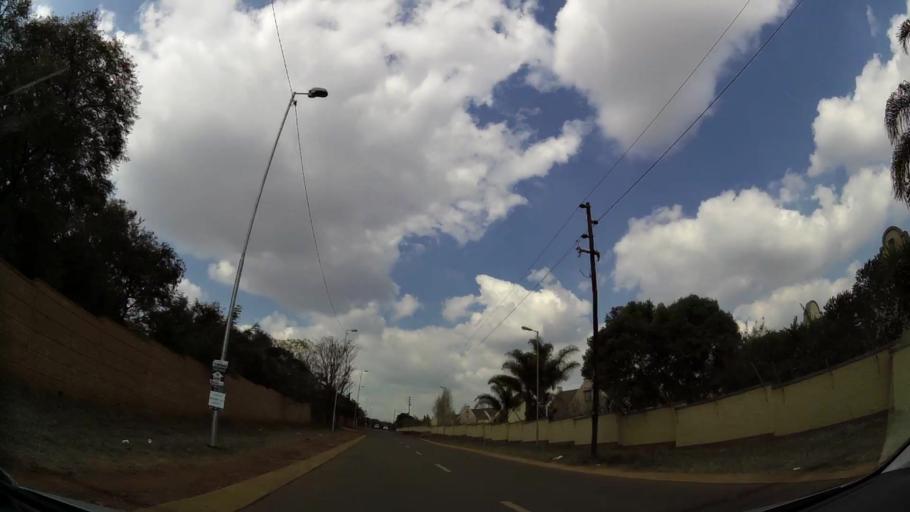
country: ZA
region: Gauteng
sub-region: City of Tshwane Metropolitan Municipality
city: Pretoria
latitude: -25.8017
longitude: 28.3441
